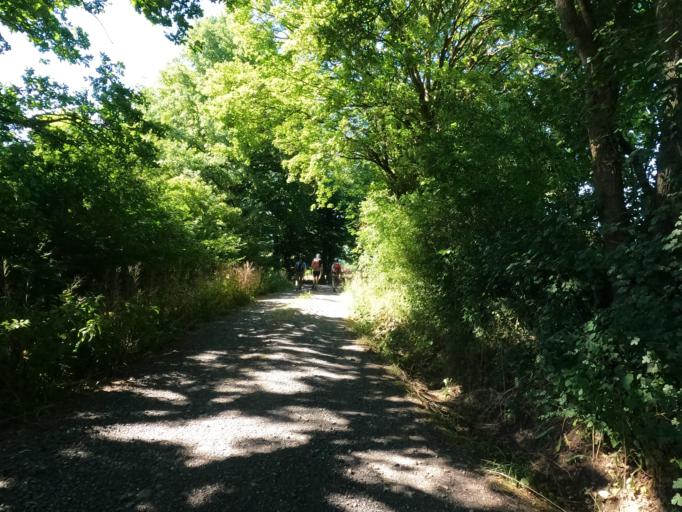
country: DE
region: Hesse
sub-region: Regierungsbezirk Darmstadt
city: Schluchtern
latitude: 50.3267
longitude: 9.5333
